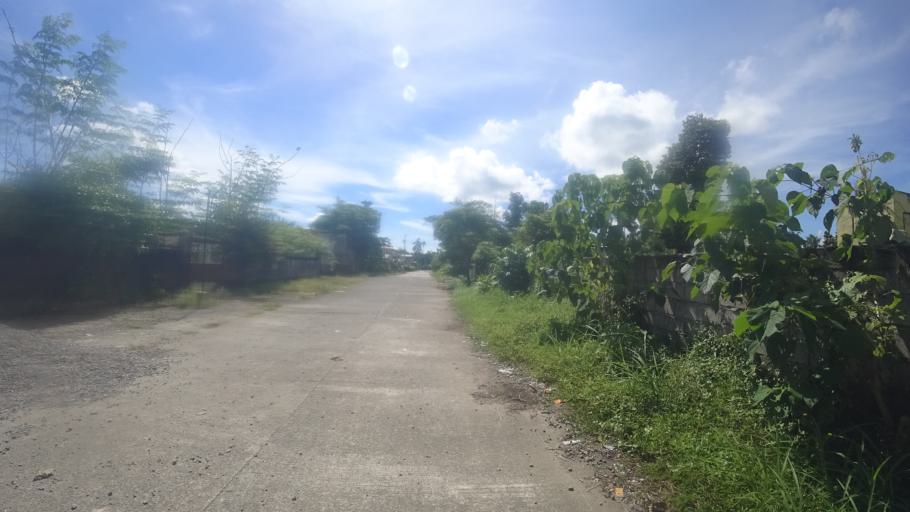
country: PH
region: Eastern Visayas
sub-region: Province of Leyte
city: Pastrana
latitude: 11.1536
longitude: 124.8593
